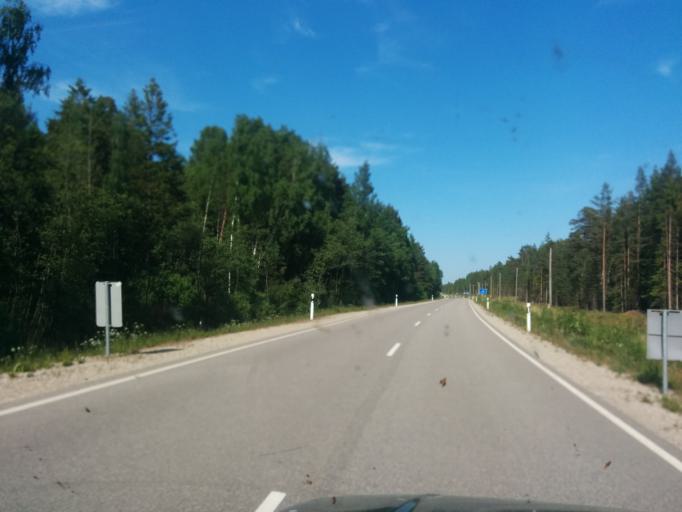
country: LV
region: Dundaga
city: Dundaga
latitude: 57.6724
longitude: 22.3156
